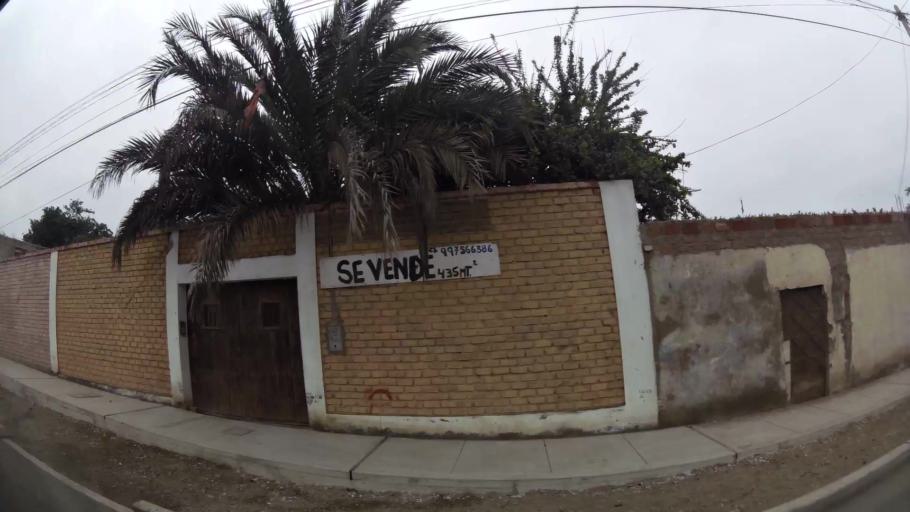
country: PE
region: Ica
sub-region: Provincia de Pisco
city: Pisco
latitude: -13.7122
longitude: -76.1966
